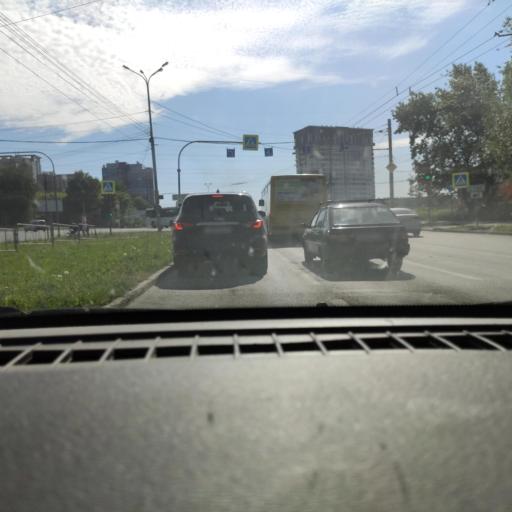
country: RU
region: Udmurtiya
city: Izhevsk
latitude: 56.8715
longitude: 53.2549
